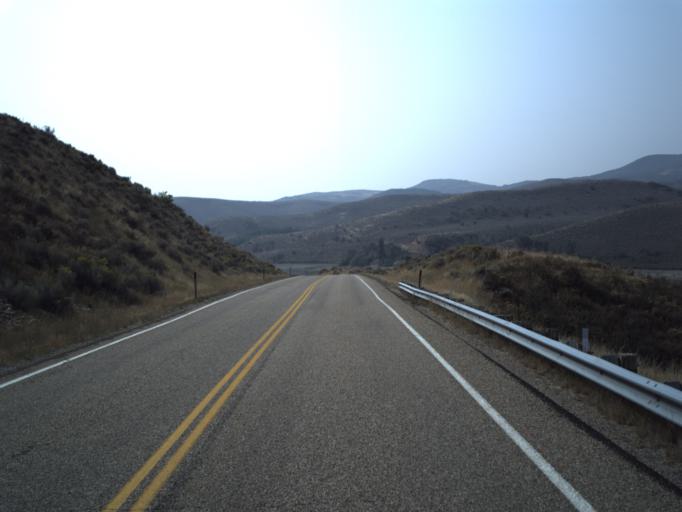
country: US
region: Utah
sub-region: Summit County
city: Summit Park
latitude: 40.9022
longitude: -111.5881
